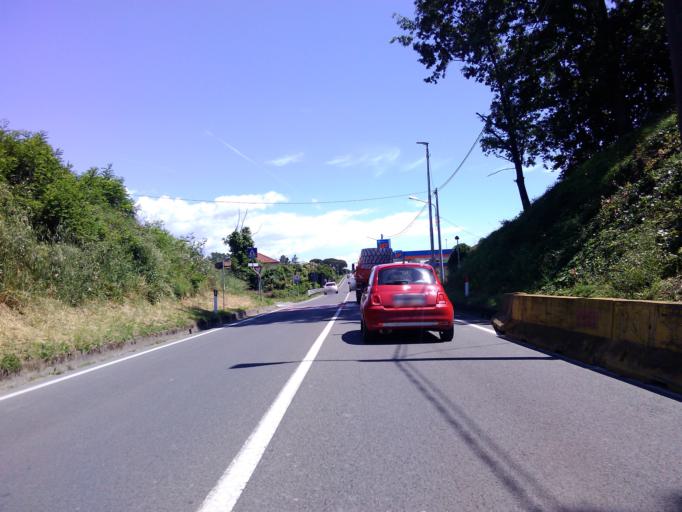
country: IT
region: Liguria
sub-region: Provincia di La Spezia
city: Santo Stefano di Magra
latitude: 44.1396
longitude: 9.9298
